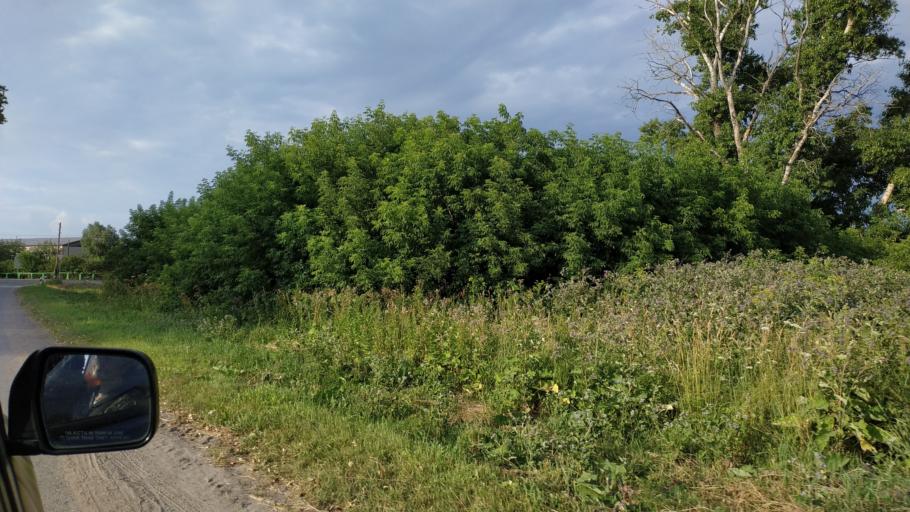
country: RU
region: Sverdlovsk
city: Yelanskiy
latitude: 57.0839
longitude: 62.4752
